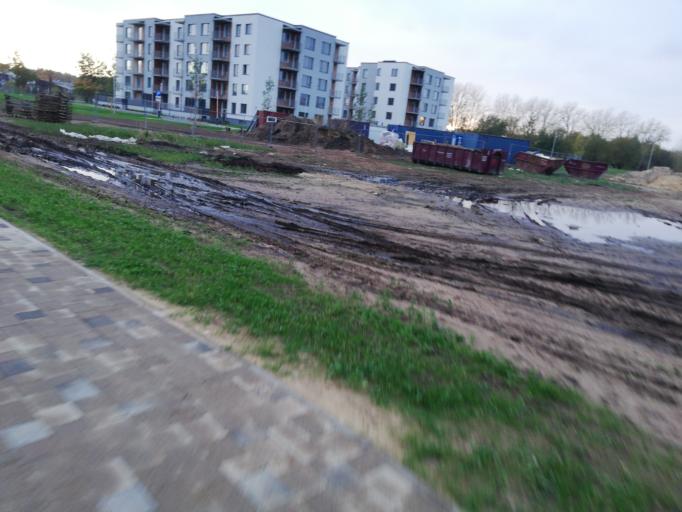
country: LV
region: Stopini
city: Ulbroka
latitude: 56.9391
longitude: 24.2261
